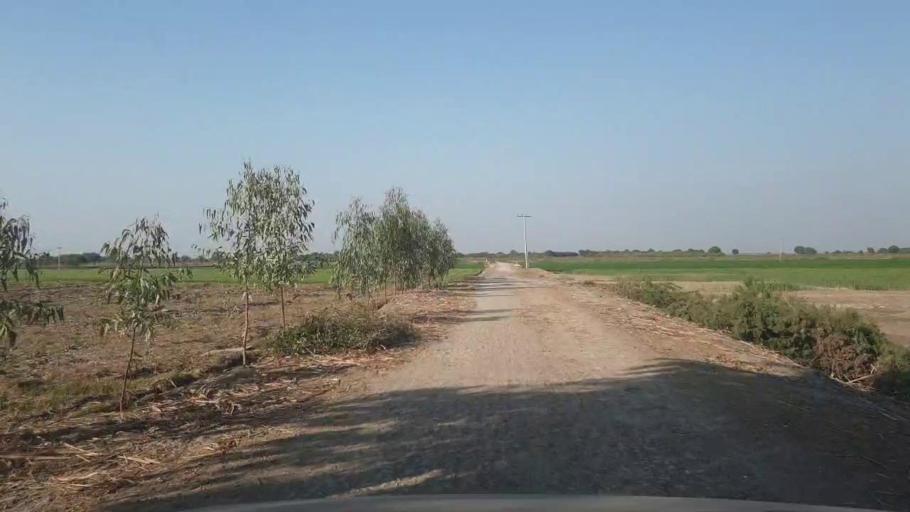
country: PK
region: Sindh
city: Chambar
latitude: 25.2963
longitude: 68.8630
